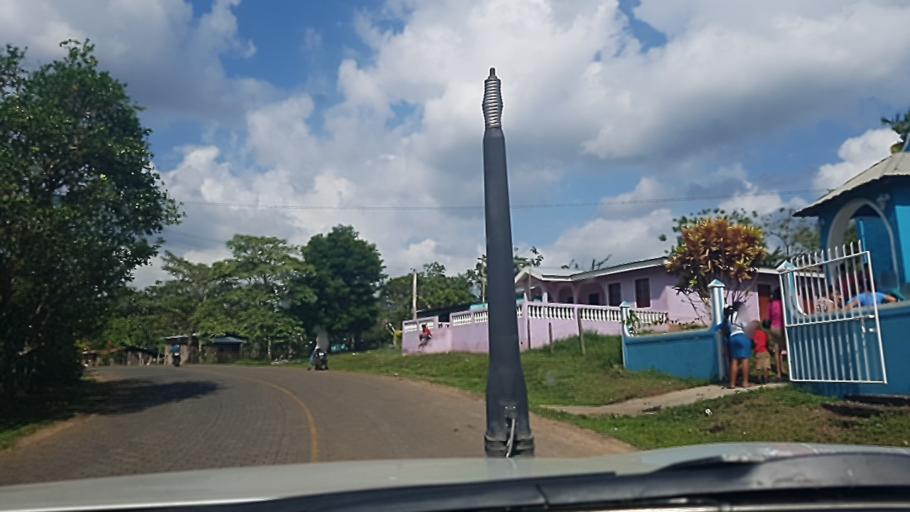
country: NI
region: Atlantico Sur
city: Nueva Guinea
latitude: 11.7020
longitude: -84.3731
